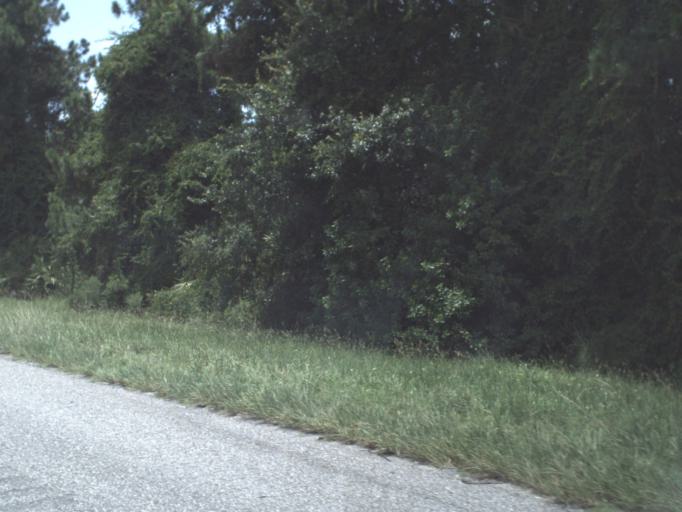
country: US
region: Florida
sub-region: Hillsborough County
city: Progress Village
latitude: 27.8820
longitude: -82.3486
